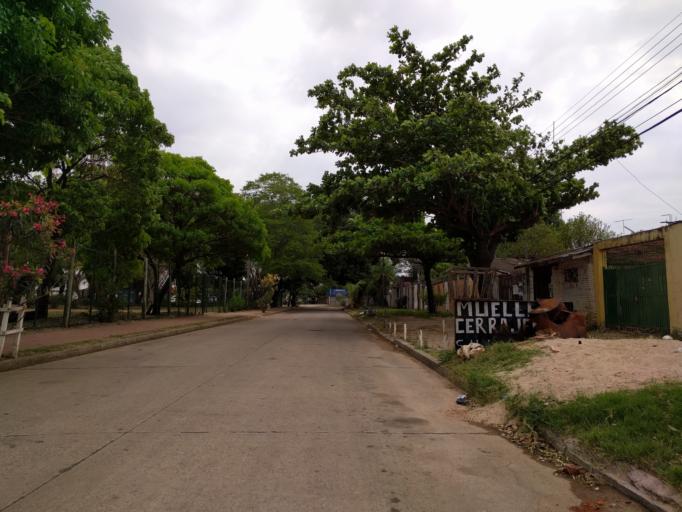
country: BO
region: Santa Cruz
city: Santa Cruz de la Sierra
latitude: -17.7919
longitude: -63.2108
